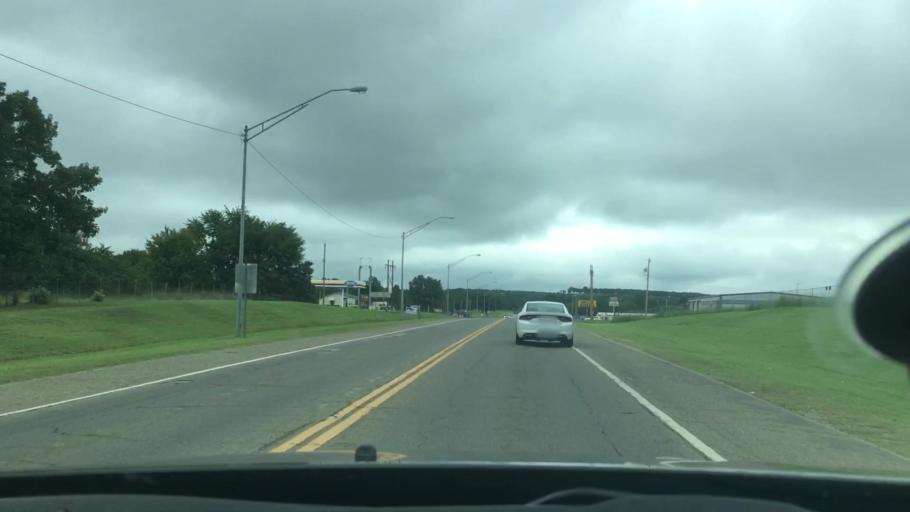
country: US
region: Oklahoma
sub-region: Sequoyah County
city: Vian
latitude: 35.5041
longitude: -94.9686
